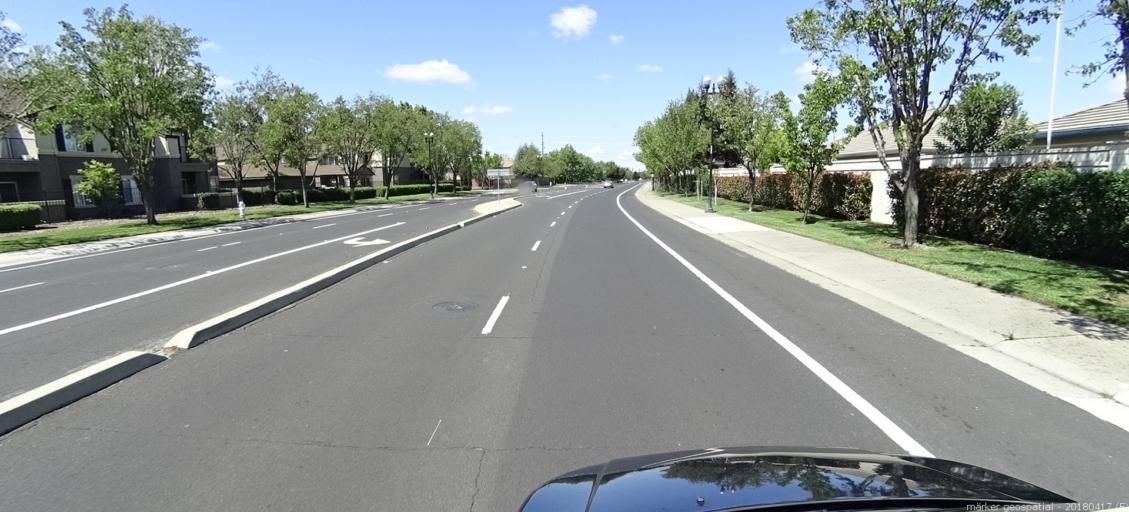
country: US
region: California
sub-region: Sacramento County
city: Laguna
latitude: 38.4146
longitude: -121.4796
